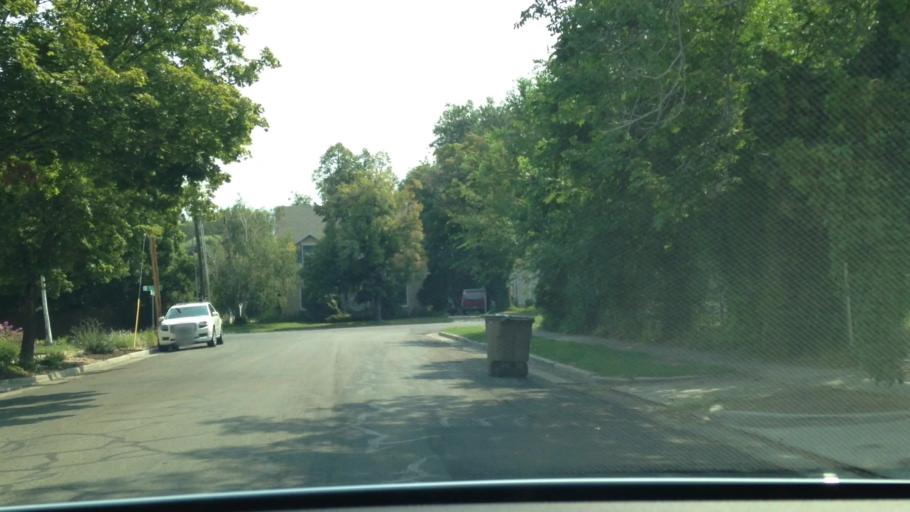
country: US
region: Utah
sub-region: Salt Lake County
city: South Salt Lake
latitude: 40.7278
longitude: -111.8689
